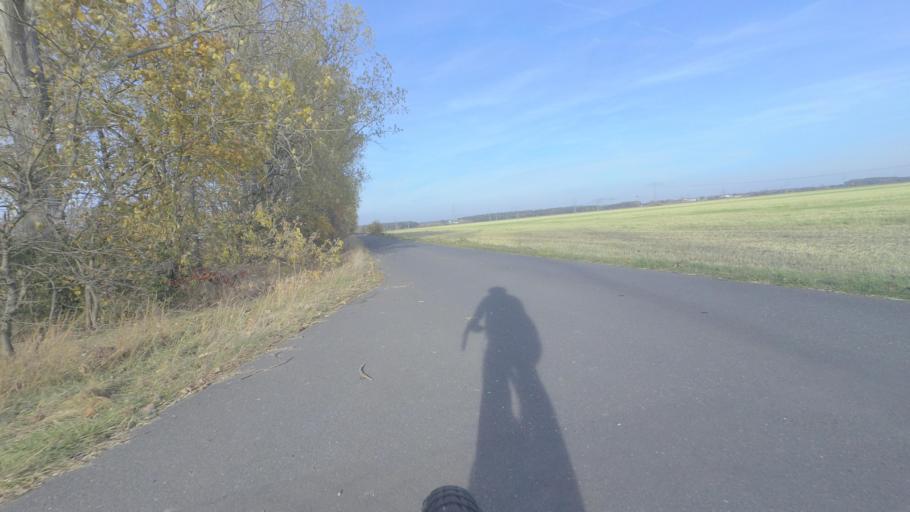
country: DE
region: Brandenburg
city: Trebbin
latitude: 52.2177
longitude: 13.2881
